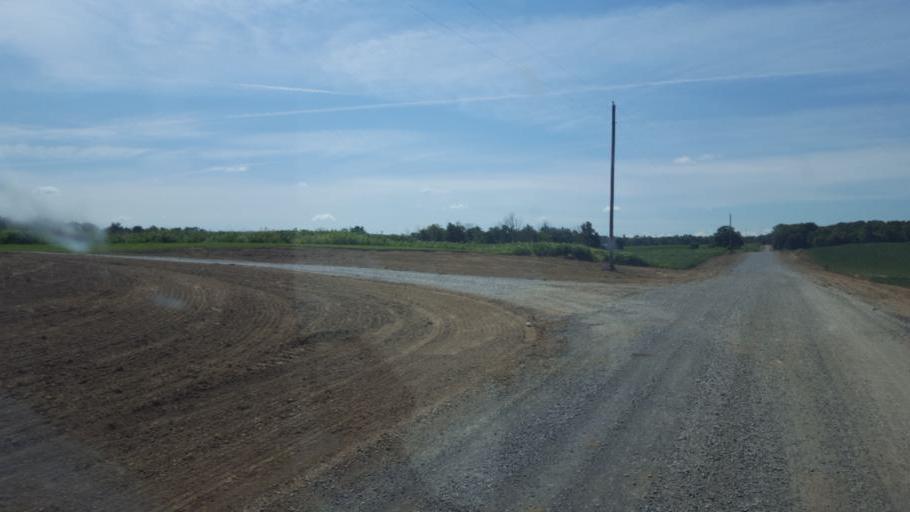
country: US
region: Ohio
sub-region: Knox County
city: Centerburg
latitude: 40.4387
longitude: -82.7177
